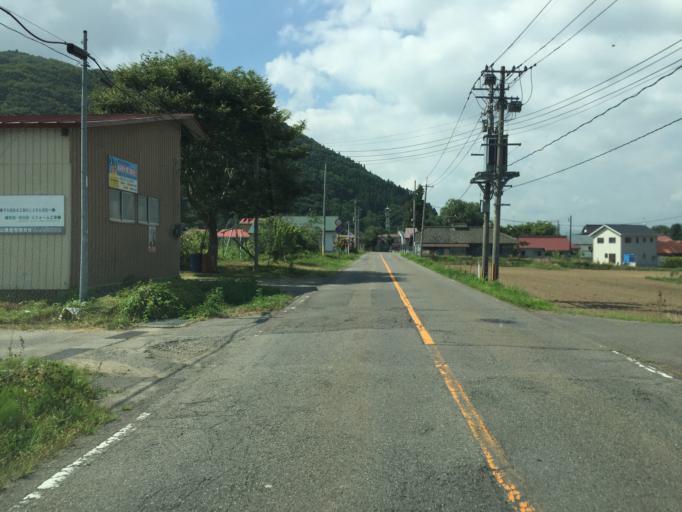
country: JP
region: Fukushima
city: Inawashiro
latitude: 37.4406
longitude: 140.1509
